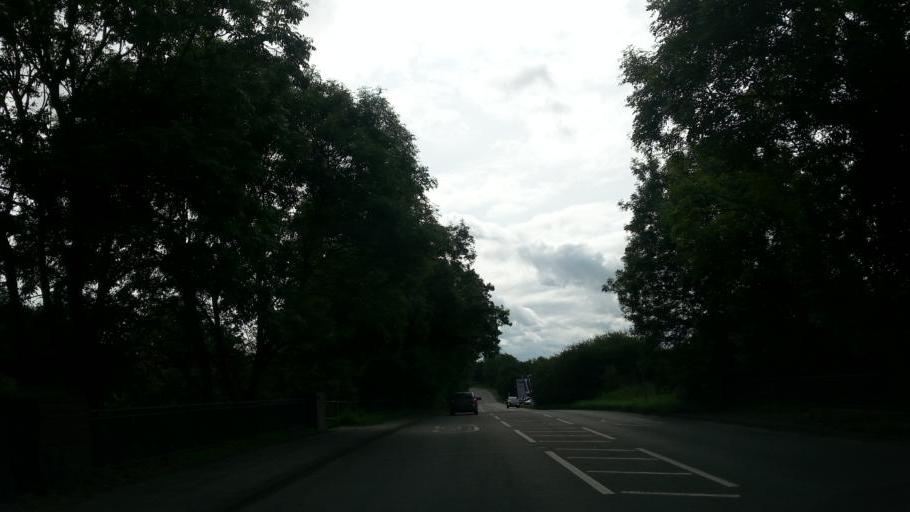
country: GB
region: England
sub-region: Leicestershire
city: Market Harborough
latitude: 52.4927
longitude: -0.9361
